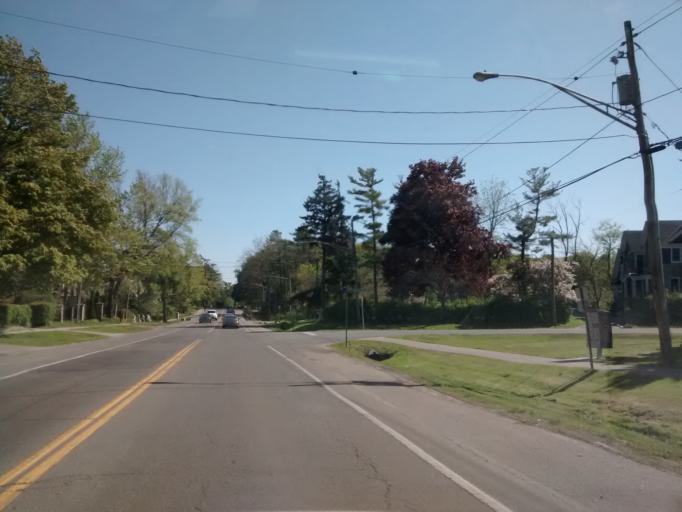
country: CA
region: Ontario
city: Oakville
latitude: 43.4150
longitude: -79.6912
